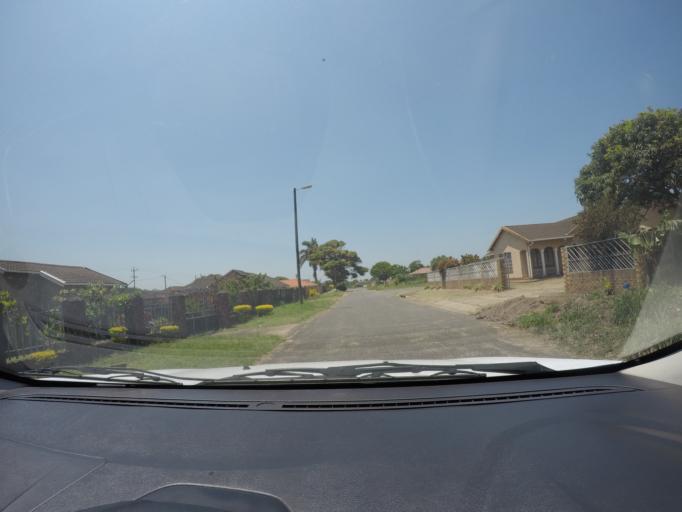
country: ZA
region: KwaZulu-Natal
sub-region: uThungulu District Municipality
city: eSikhawini
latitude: -28.8873
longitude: 31.8842
